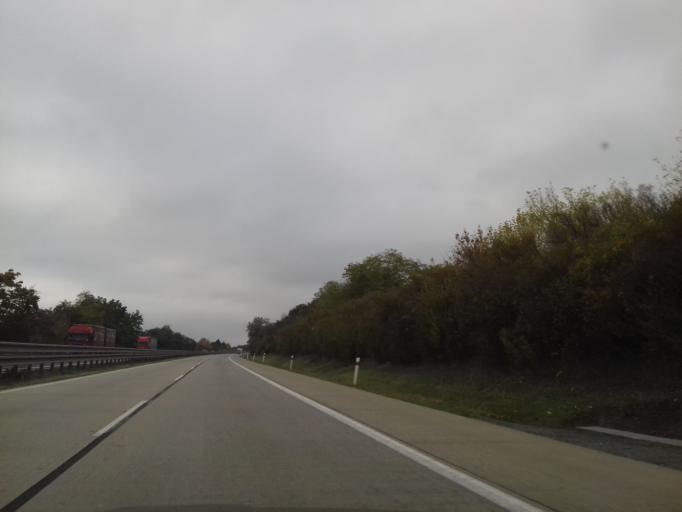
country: CZ
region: South Moravian
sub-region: Okres Breclav
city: Hustopece
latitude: 48.9330
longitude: 16.7492
